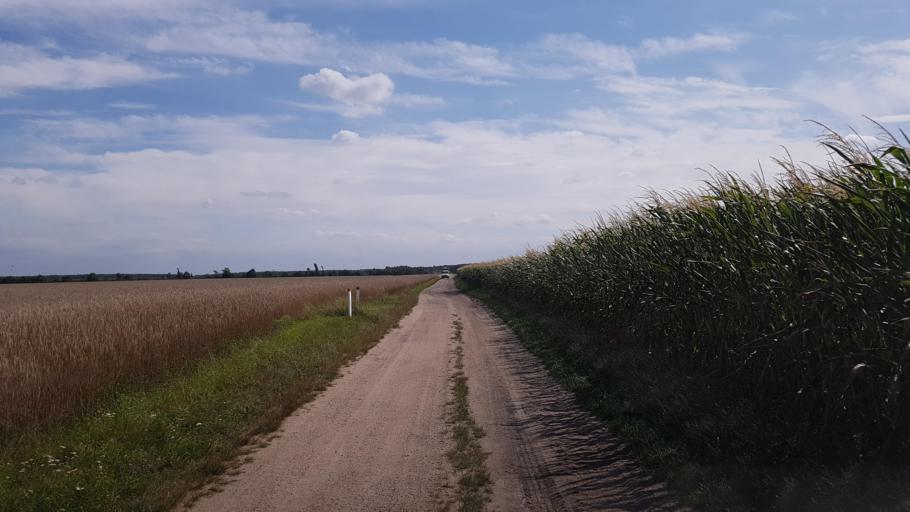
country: DE
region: Brandenburg
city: Muhlberg
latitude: 51.4626
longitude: 13.2820
